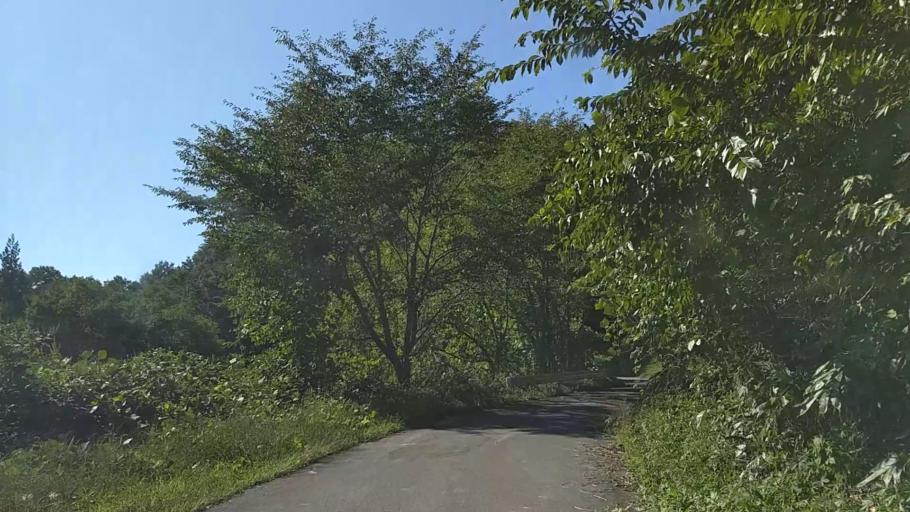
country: JP
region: Nagano
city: Nagano-shi
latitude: 36.5907
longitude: 138.0843
